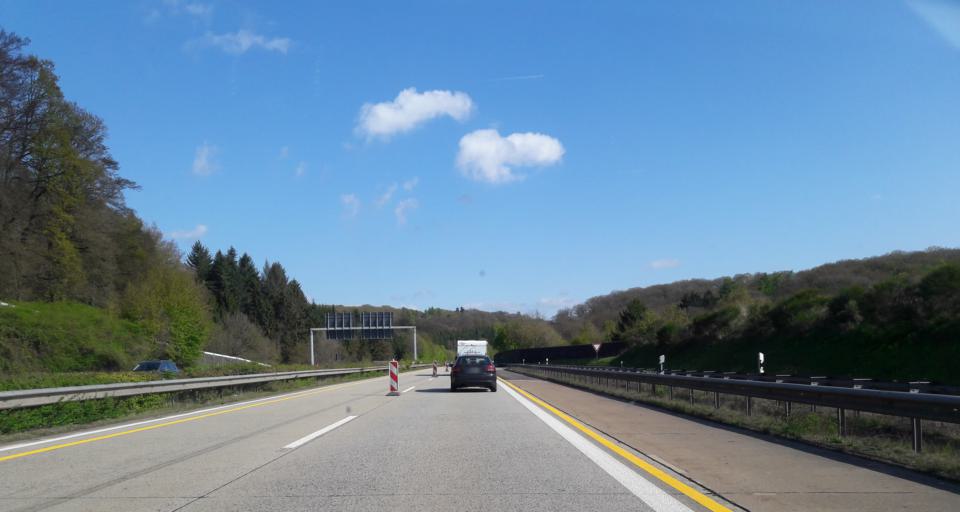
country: DE
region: Rheinland-Pfalz
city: Altrich
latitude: 49.9527
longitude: 6.8830
